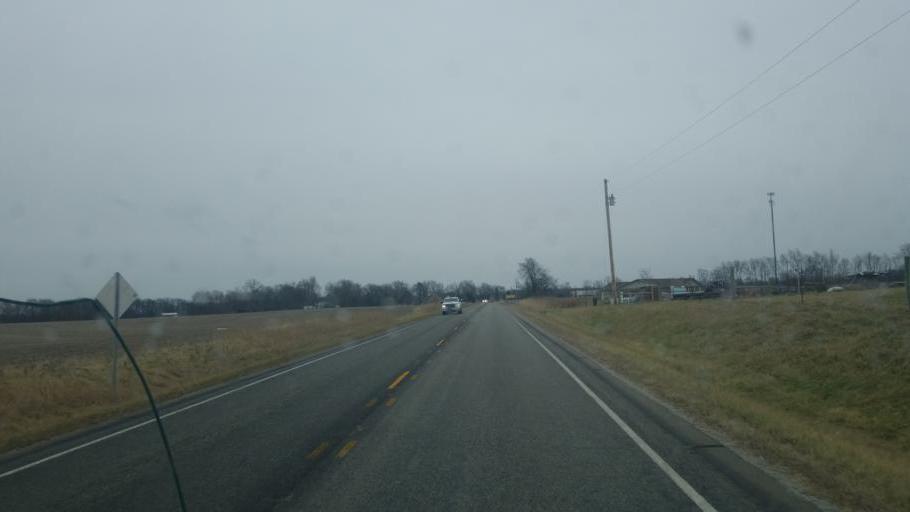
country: US
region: Indiana
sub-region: Henry County
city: Knightstown
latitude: 39.8273
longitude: -85.5402
